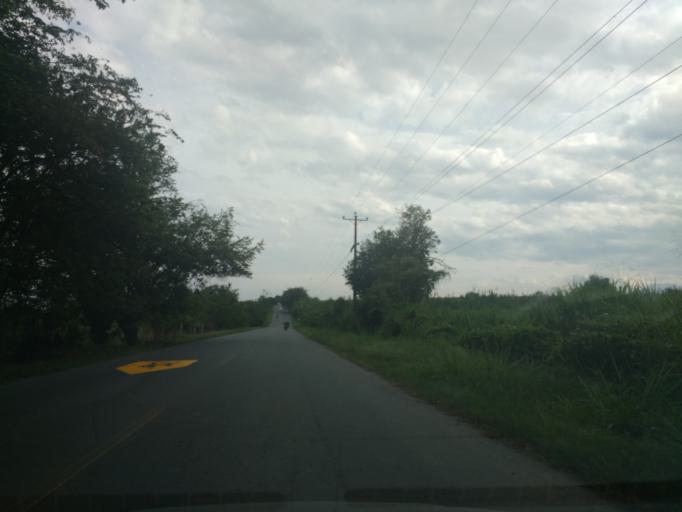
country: CO
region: Valle del Cauca
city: Florida
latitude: 3.2880
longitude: -76.2261
